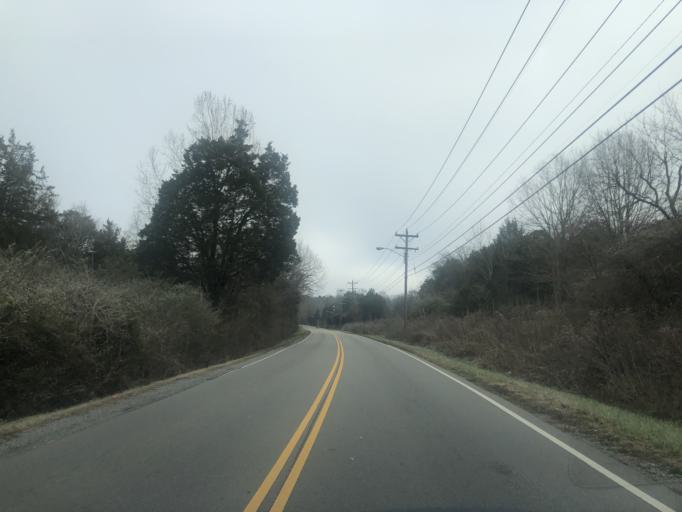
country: US
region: Tennessee
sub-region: Rutherford County
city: La Vergne
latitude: 36.0603
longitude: -86.6669
